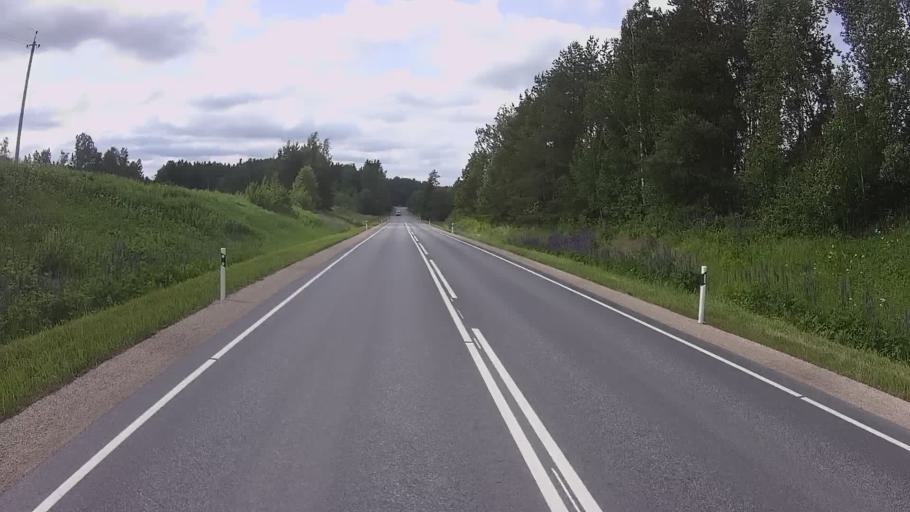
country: EE
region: Polvamaa
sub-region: Polva linn
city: Polva
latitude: 58.0483
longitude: 27.0753
